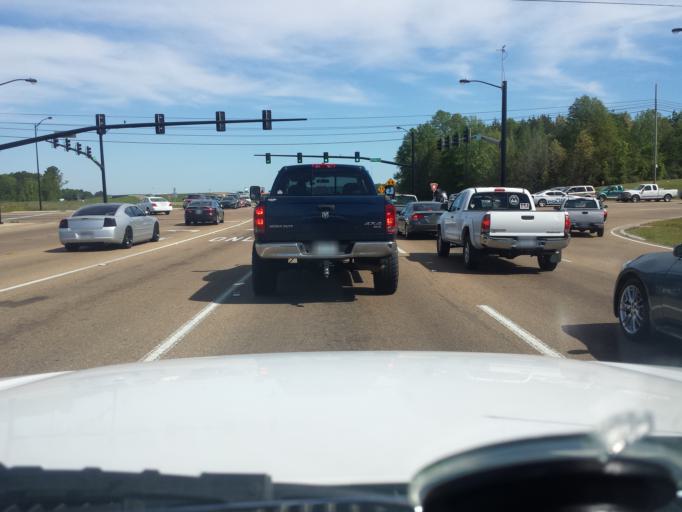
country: US
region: Mississippi
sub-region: Rankin County
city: Pearl
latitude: 32.2832
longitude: -90.0741
